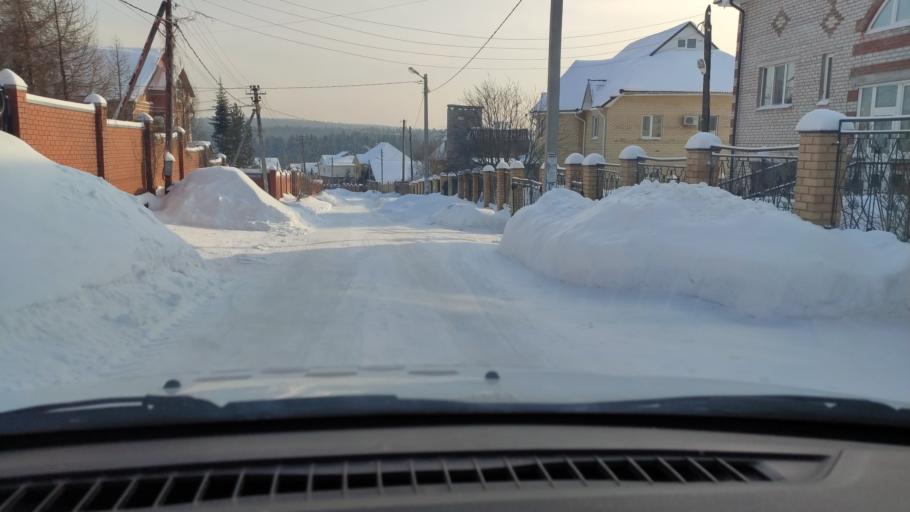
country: RU
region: Perm
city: Perm
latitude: 58.0371
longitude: 56.3921
